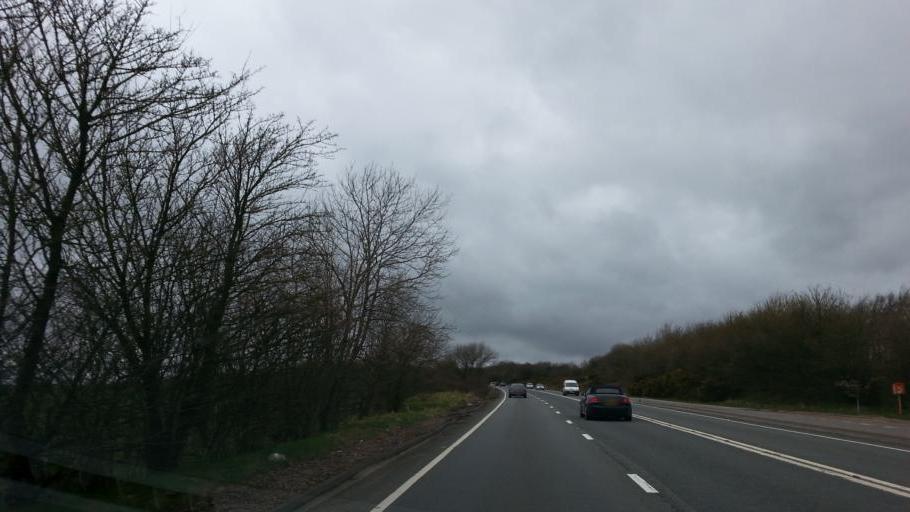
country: GB
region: England
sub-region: Devon
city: Tiverton
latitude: 50.9352
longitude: -3.5456
